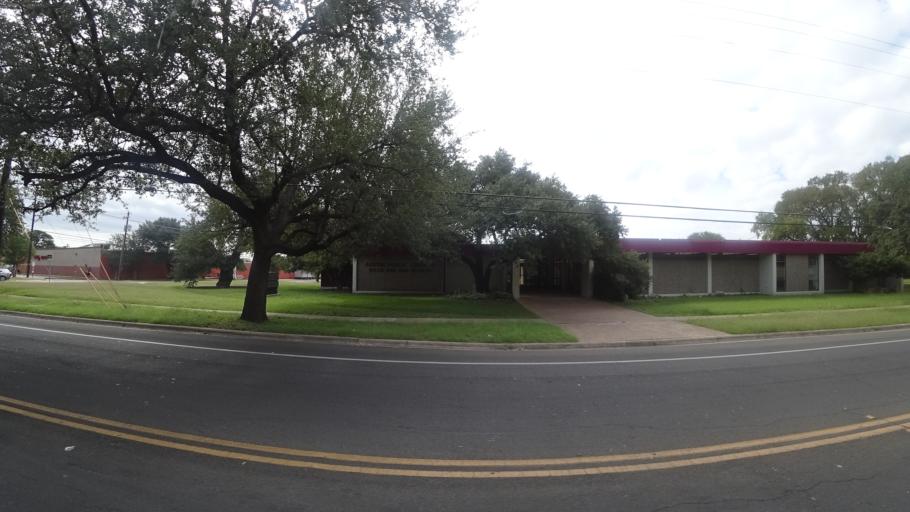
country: US
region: Texas
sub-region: Travis County
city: Austin
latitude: 30.2734
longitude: -97.6995
